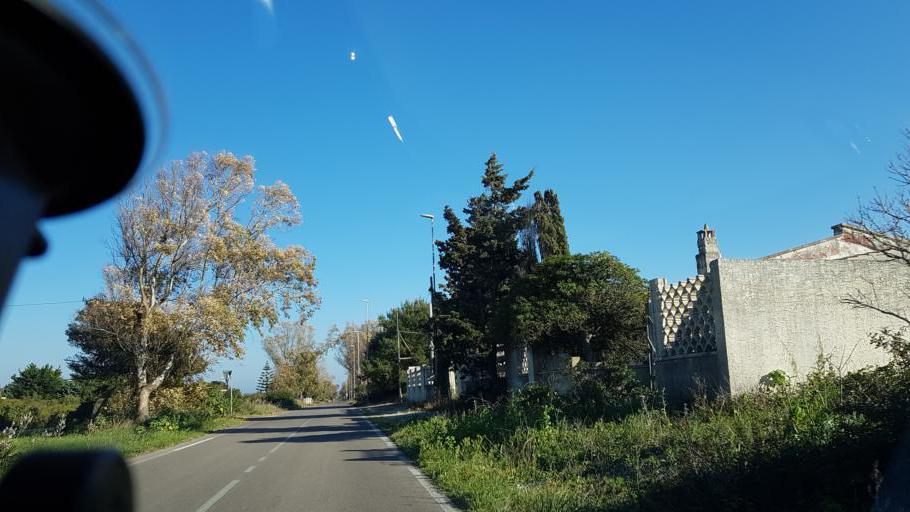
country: IT
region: Apulia
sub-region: Provincia di Lecce
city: Giorgilorio
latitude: 40.4547
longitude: 18.2145
